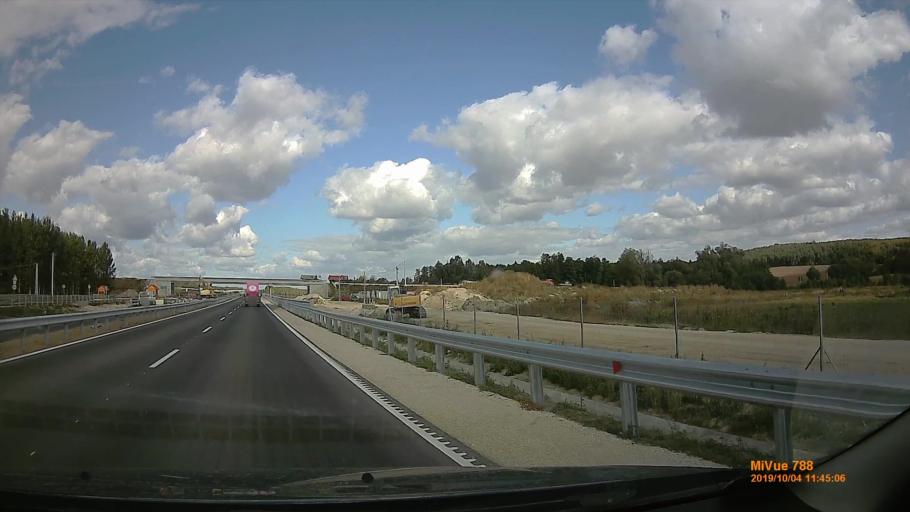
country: HU
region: Somogy
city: Karad
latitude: 46.6218
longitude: 17.7956
